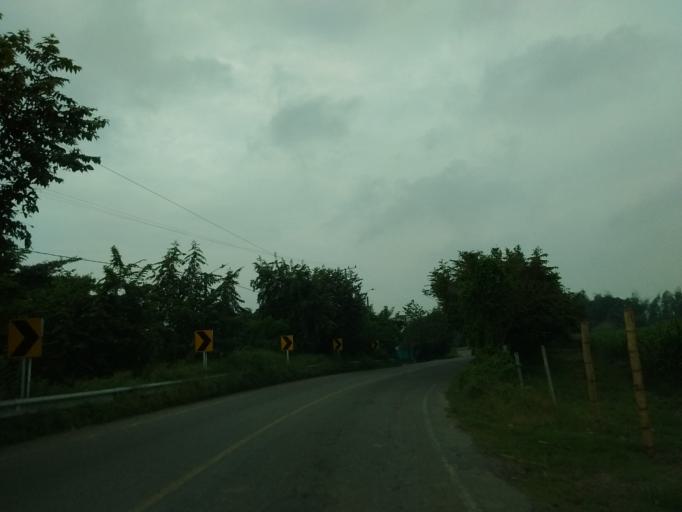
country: CO
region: Cauca
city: Puerto Tejada
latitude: 3.2203
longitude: -76.3947
